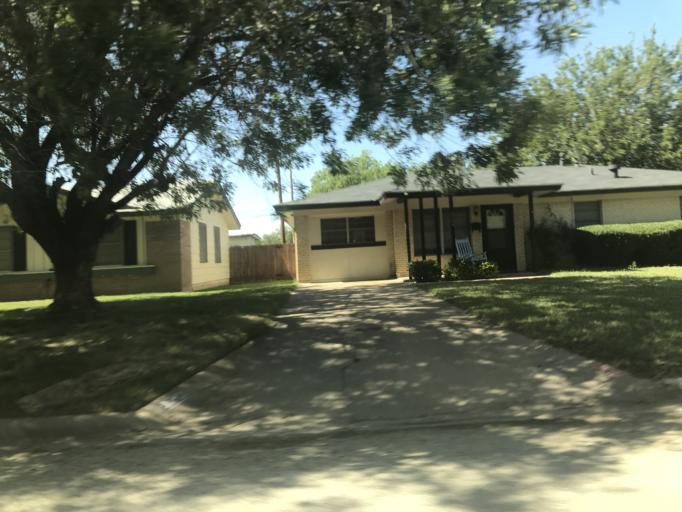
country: US
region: Texas
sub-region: Taylor County
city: Abilene
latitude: 32.4088
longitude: -99.7507
